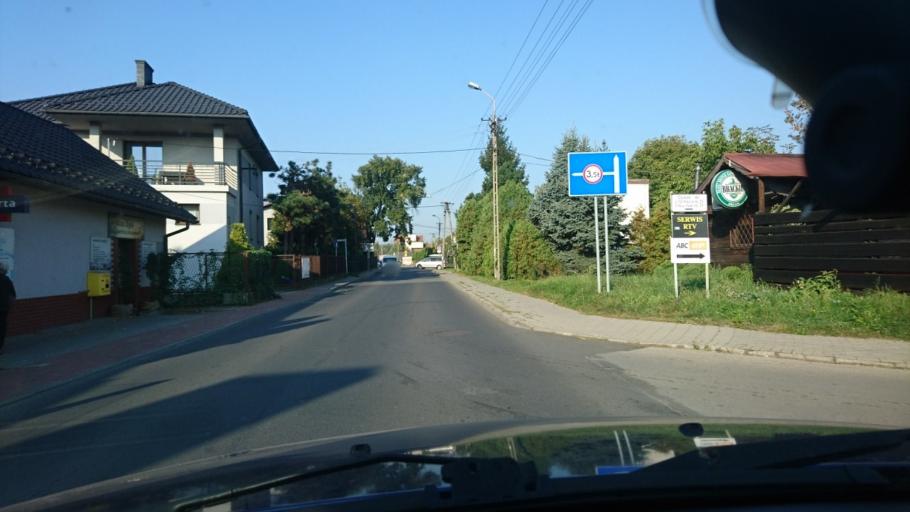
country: PL
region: Silesian Voivodeship
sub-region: Bielsko-Biala
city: Bielsko-Biala
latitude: 49.8533
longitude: 19.0460
